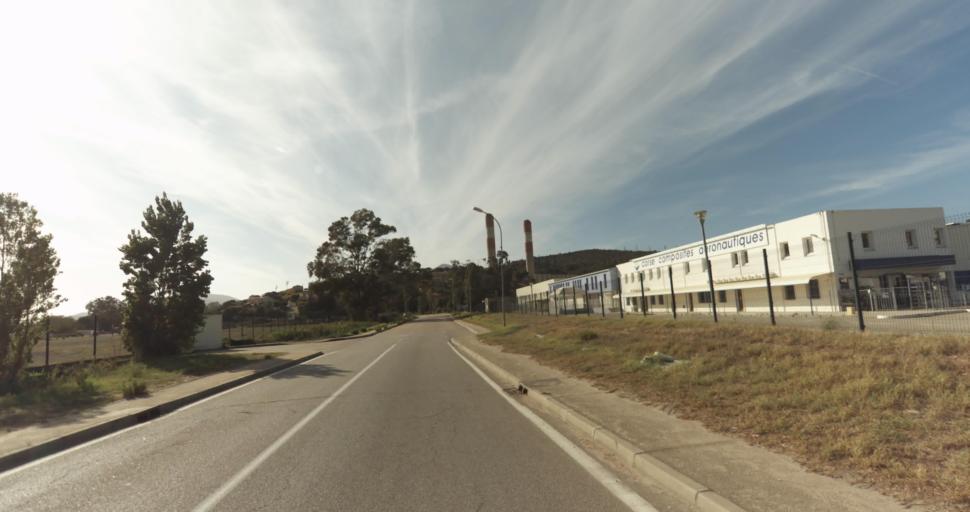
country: FR
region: Corsica
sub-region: Departement de la Corse-du-Sud
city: Ajaccio
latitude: 41.9302
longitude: 8.7868
